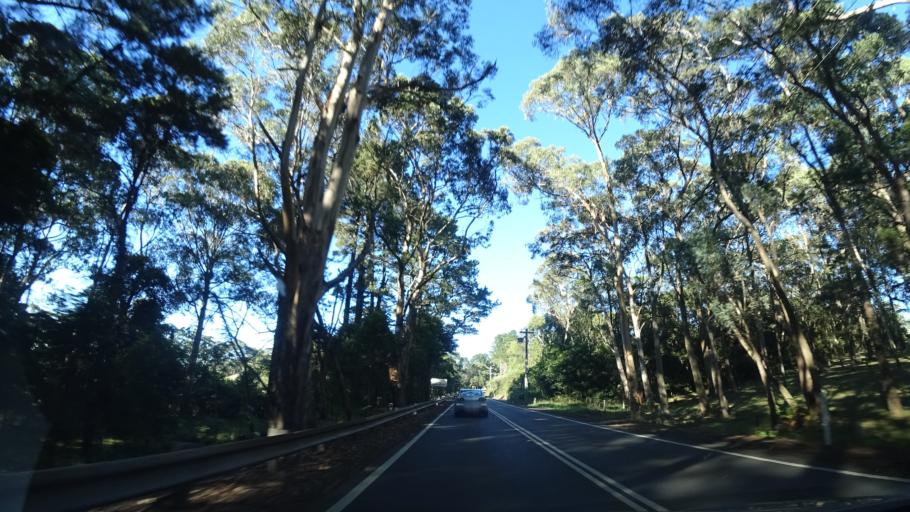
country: AU
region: New South Wales
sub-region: Blue Mountains Municipality
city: Lawson
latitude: -33.5339
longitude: 150.4449
